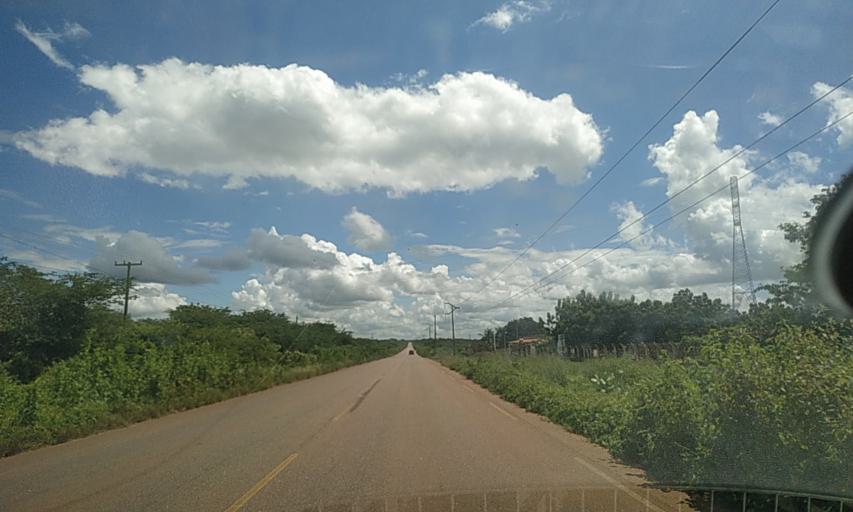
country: BR
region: Rio Grande do Norte
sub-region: Mossoro
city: Mossoro
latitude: -5.1627
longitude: -37.4279
